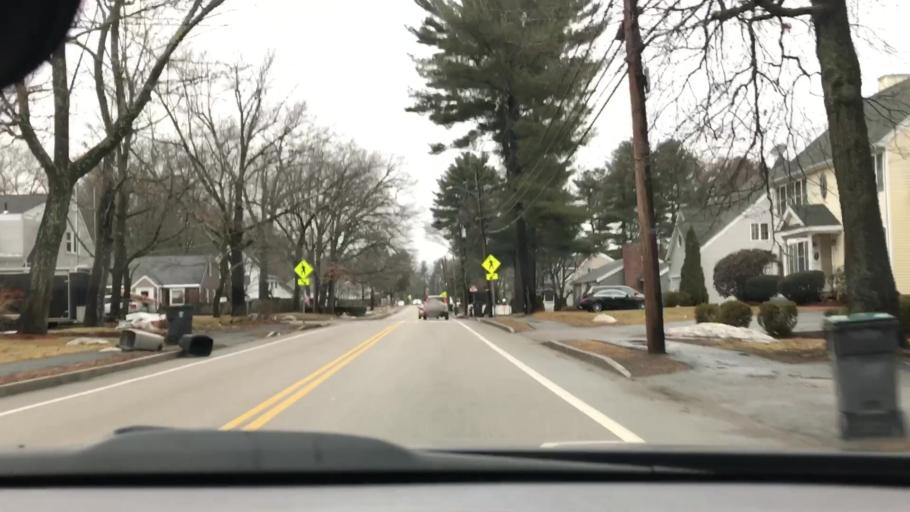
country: US
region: Massachusetts
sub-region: Middlesex County
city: Natick
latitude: 42.3074
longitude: -71.3330
